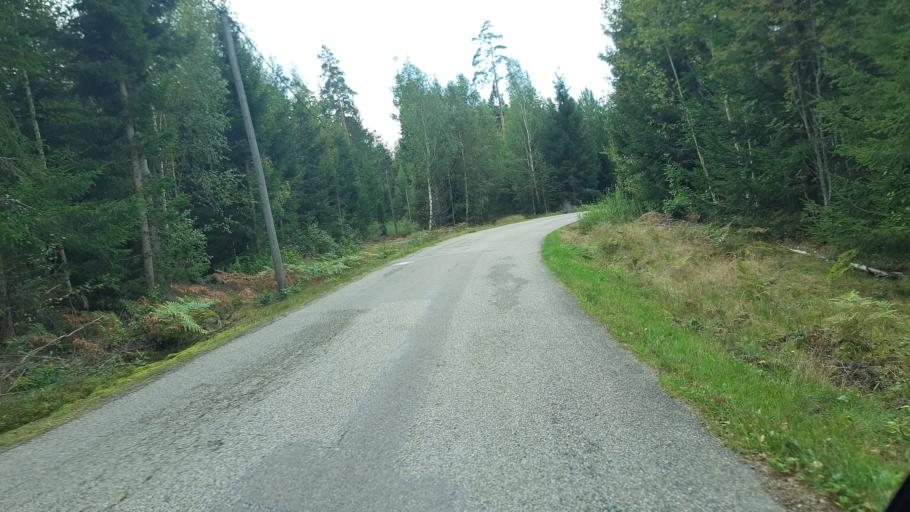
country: SE
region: Kronoberg
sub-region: Tingsryds Kommun
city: Tingsryd
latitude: 56.4753
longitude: 15.1609
